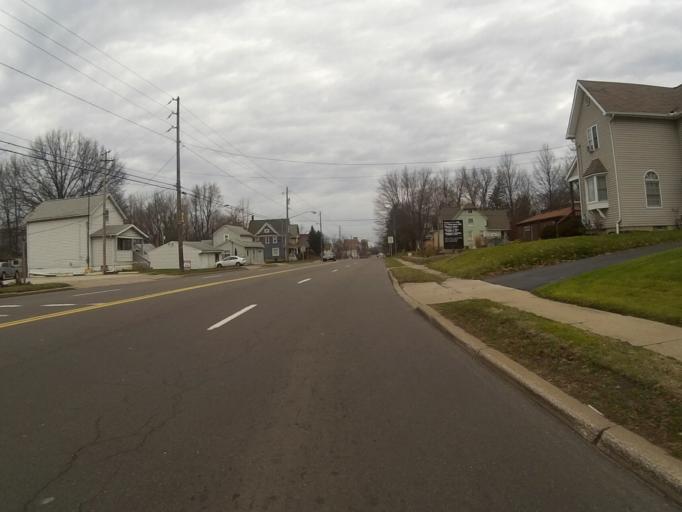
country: US
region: Ohio
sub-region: Portage County
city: Kent
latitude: 41.1437
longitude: -81.3582
